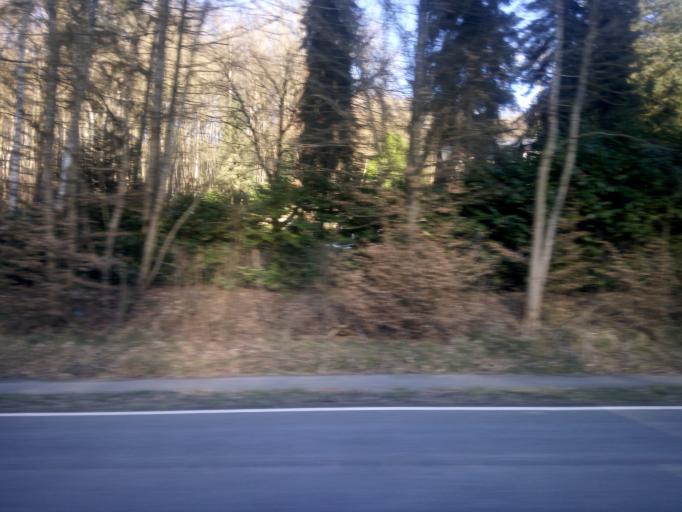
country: LU
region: Luxembourg
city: Kirchberg
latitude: 49.6393
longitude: 6.1514
